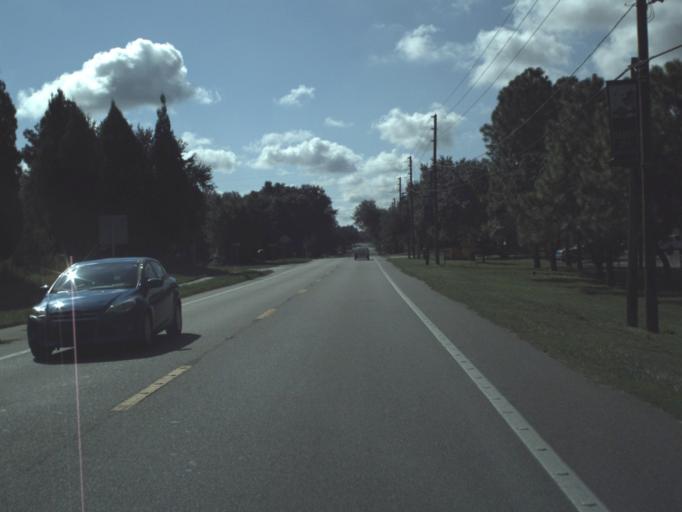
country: US
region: Florida
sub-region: Polk County
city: Babson Park
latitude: 27.8387
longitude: -81.5306
